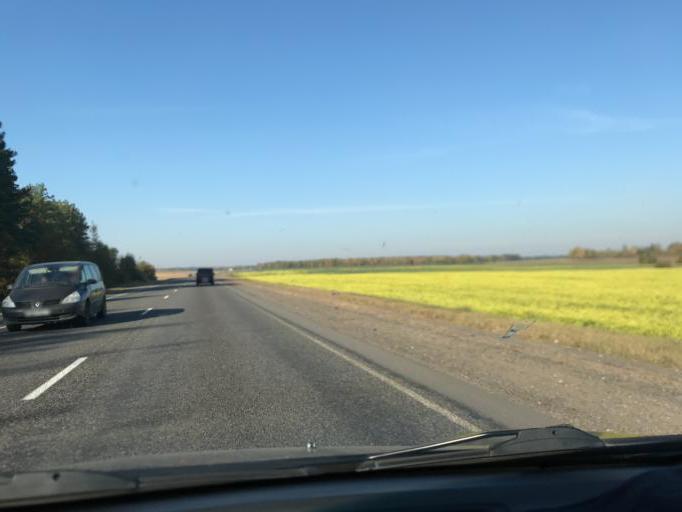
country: BY
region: Mogilev
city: Babruysk
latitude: 53.0860
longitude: 29.0640
